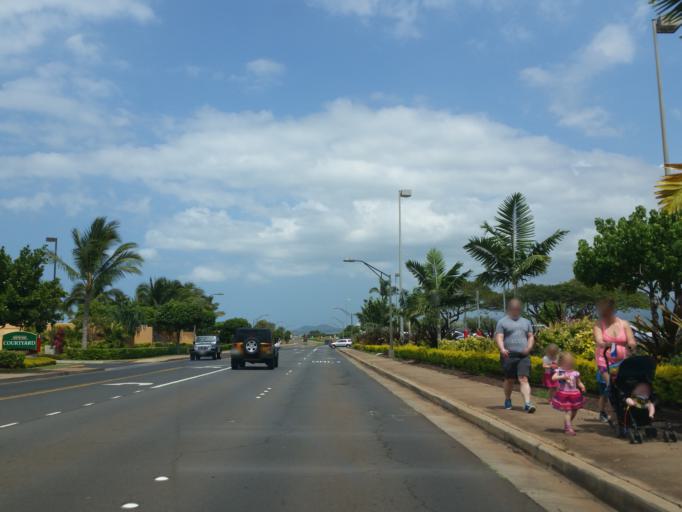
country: US
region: Hawaii
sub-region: Maui County
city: Kahului
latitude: 20.8879
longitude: -156.4504
